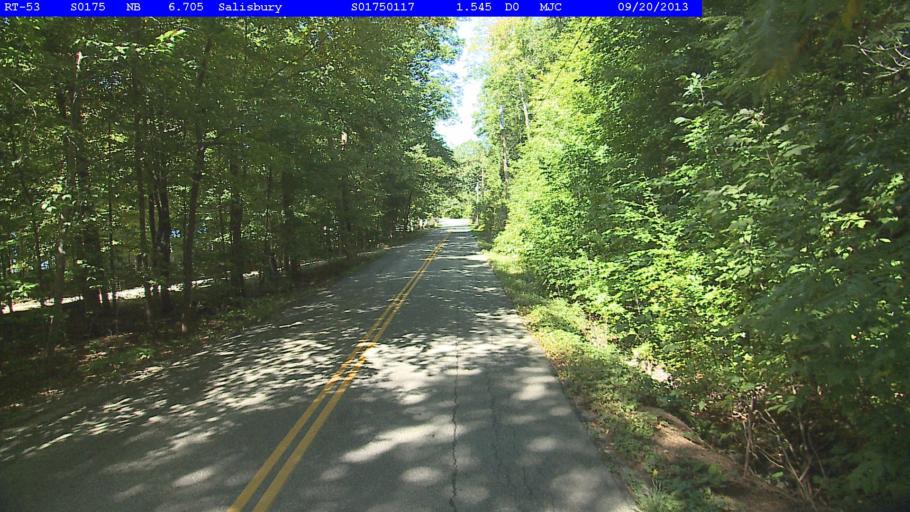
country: US
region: Vermont
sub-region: Rutland County
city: Brandon
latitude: 43.9201
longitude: -73.0710
